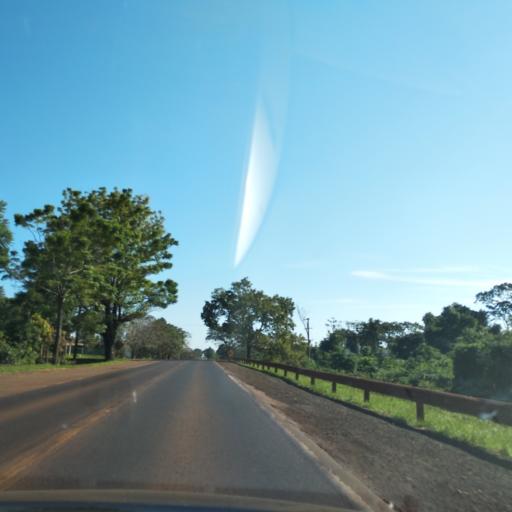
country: AR
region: Misiones
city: Jardin America
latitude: -27.0551
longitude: -55.2534
